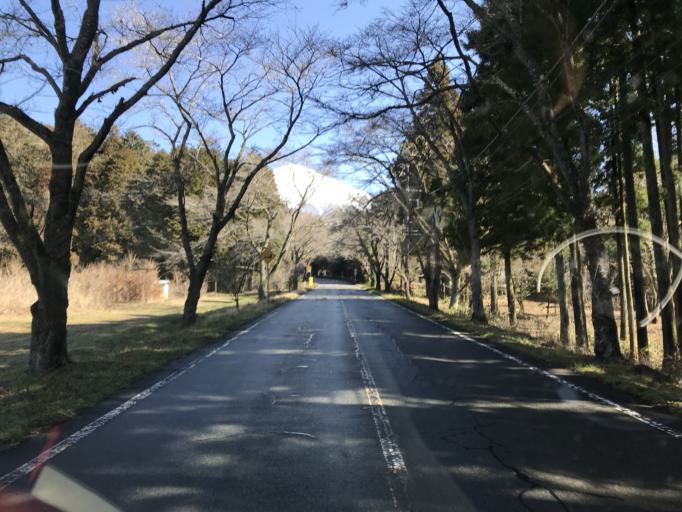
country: JP
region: Shizuoka
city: Fujinomiya
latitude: 35.2805
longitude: 138.6606
